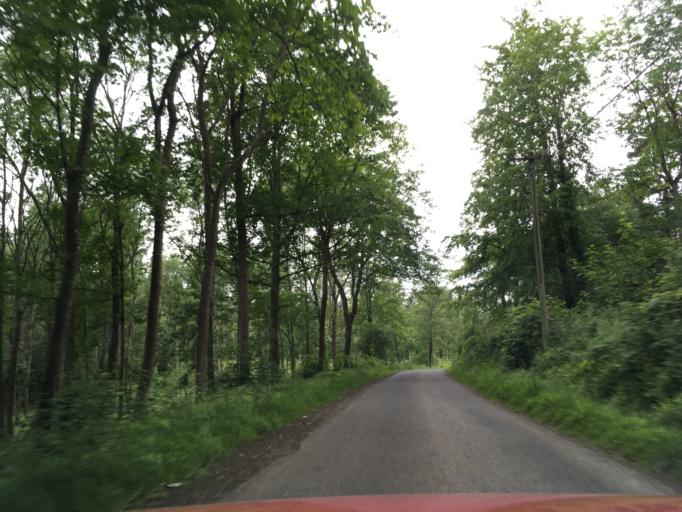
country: GB
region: England
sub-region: Wiltshire
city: Luckington
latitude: 51.5739
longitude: -2.2851
